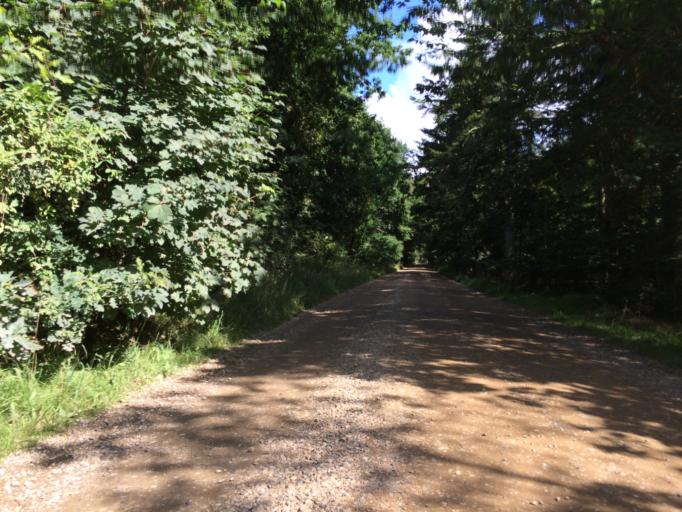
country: DK
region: Central Jutland
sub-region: Holstebro Kommune
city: Ulfborg
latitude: 56.2840
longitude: 8.1682
